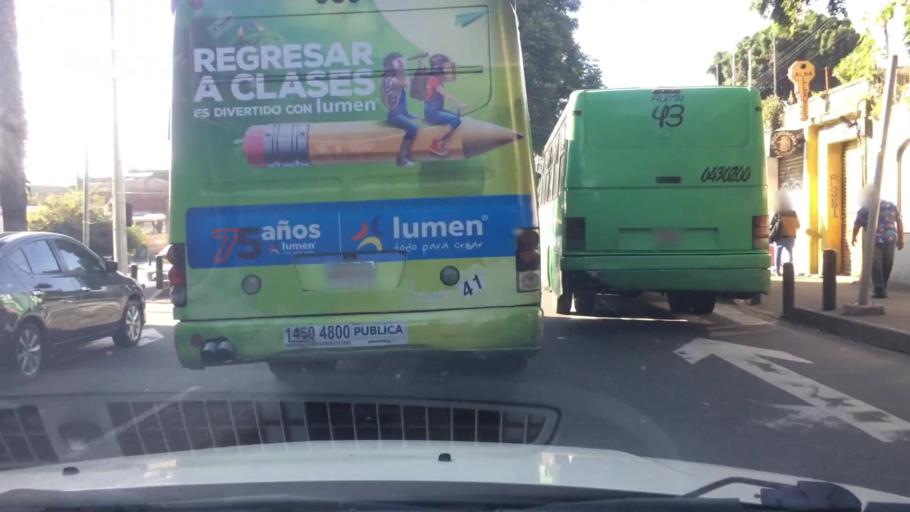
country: MX
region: Mexico City
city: Alvaro Obregon
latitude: 19.3473
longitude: -99.1907
